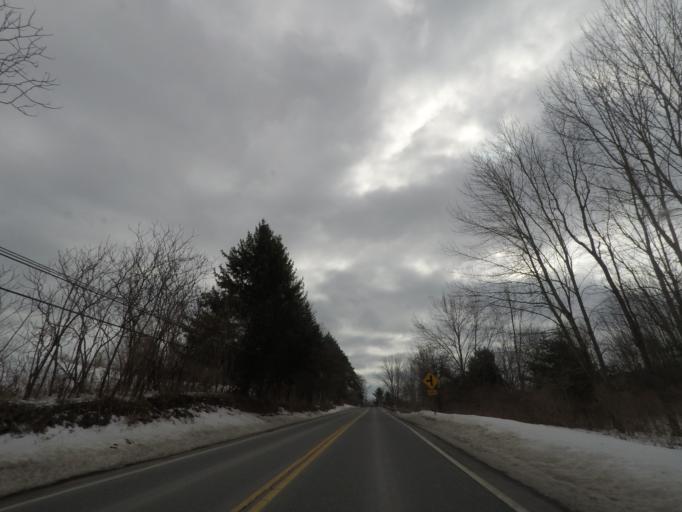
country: US
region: New York
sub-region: Washington County
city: Greenwich
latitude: 43.0737
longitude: -73.4822
